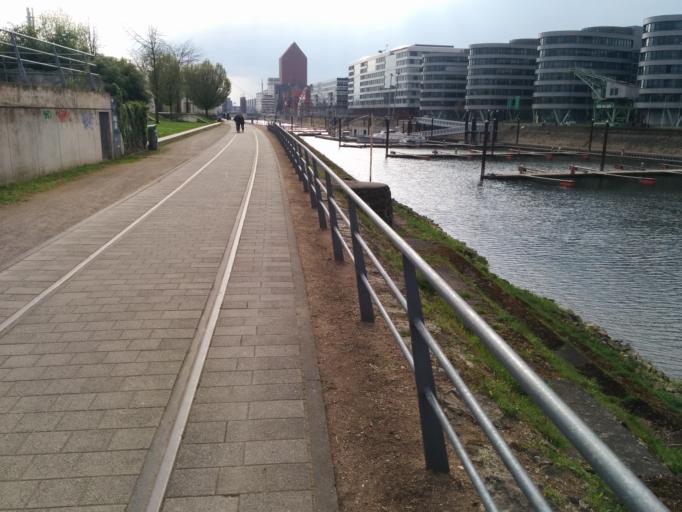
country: DE
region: North Rhine-Westphalia
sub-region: Regierungsbezirk Dusseldorf
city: Duisburg
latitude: 51.4399
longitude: 6.7670
